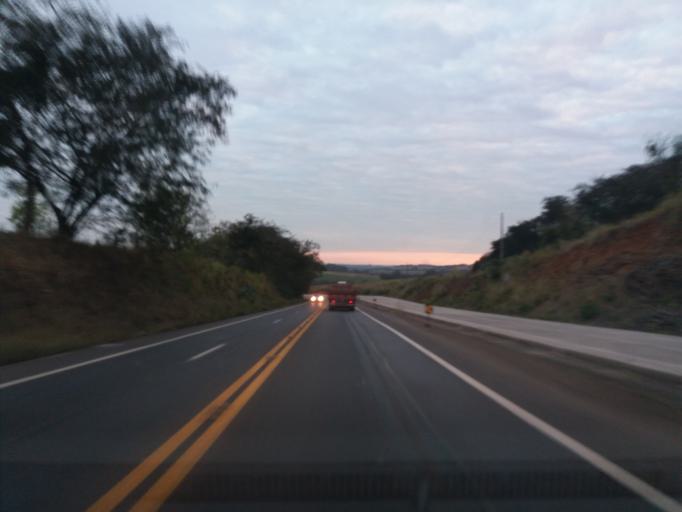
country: BR
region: Parana
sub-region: Realeza
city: Realeza
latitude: -25.3798
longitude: -53.5763
